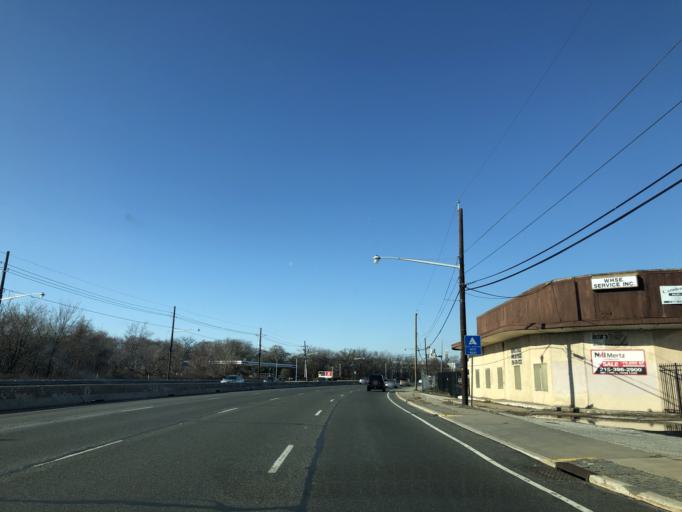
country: US
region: New Jersey
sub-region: Camden County
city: Camden
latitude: 39.9410
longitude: -75.1017
